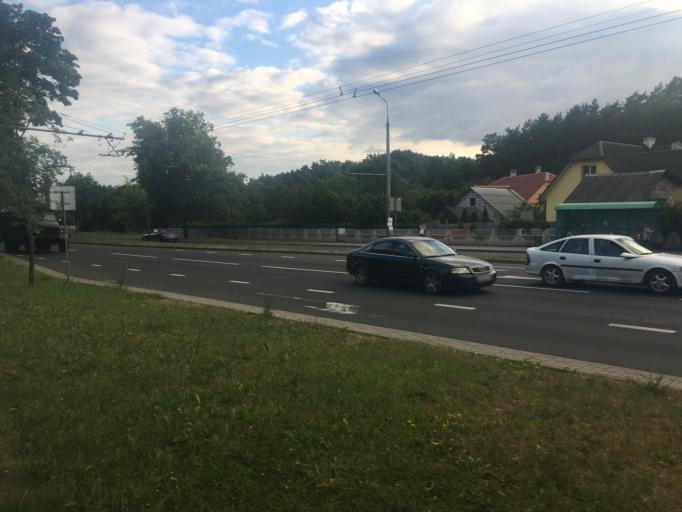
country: BY
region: Grodnenskaya
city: Hrodna
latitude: 53.6892
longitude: 23.8010
